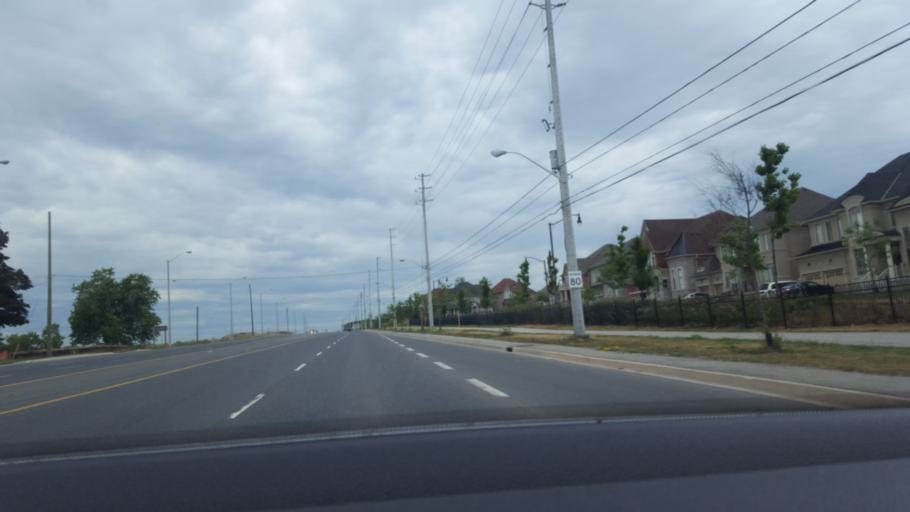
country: CA
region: Ontario
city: Brampton
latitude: 43.6513
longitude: -79.8083
